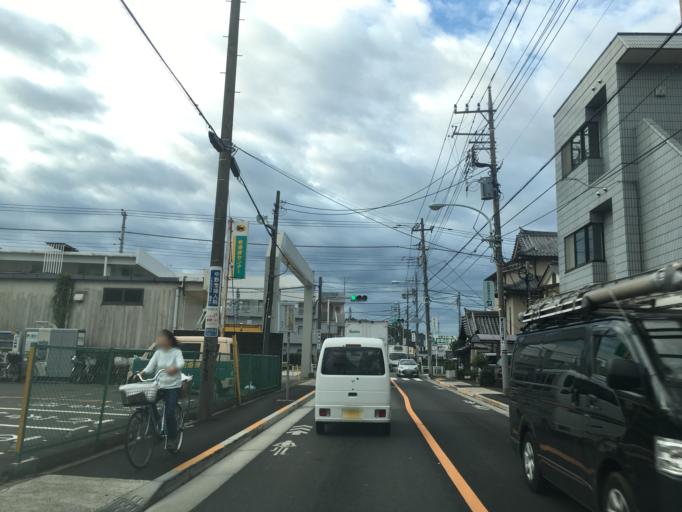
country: JP
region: Tokyo
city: Kokubunji
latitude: 35.7264
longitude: 139.4655
